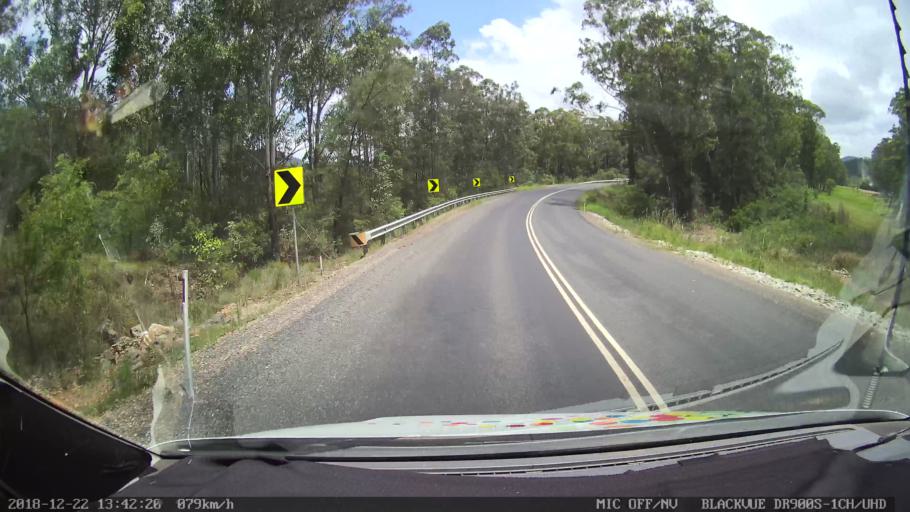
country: AU
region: New South Wales
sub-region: Clarence Valley
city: Coutts Crossing
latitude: -29.9224
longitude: 152.7544
